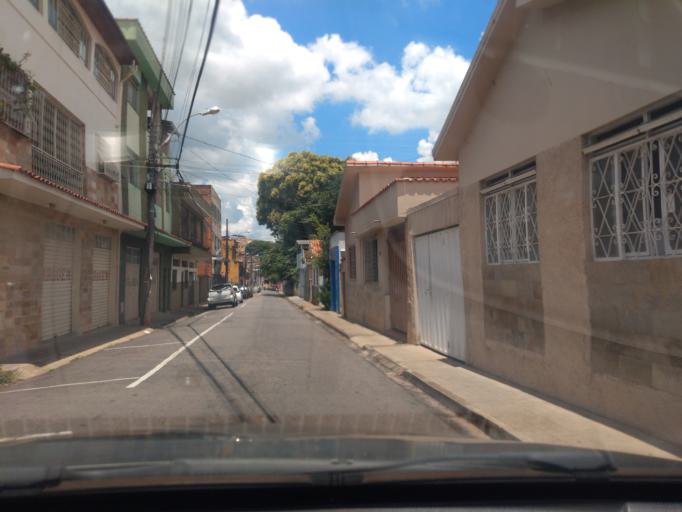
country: BR
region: Minas Gerais
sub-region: Tres Coracoes
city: Tres Coracoes
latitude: -21.6919
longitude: -45.2574
